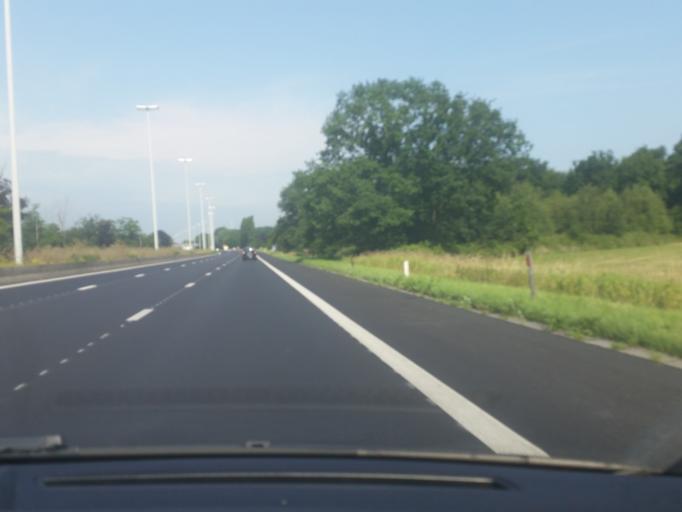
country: BE
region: Flanders
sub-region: Provincie West-Vlaanderen
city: Beernem
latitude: 51.1100
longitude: 3.3624
